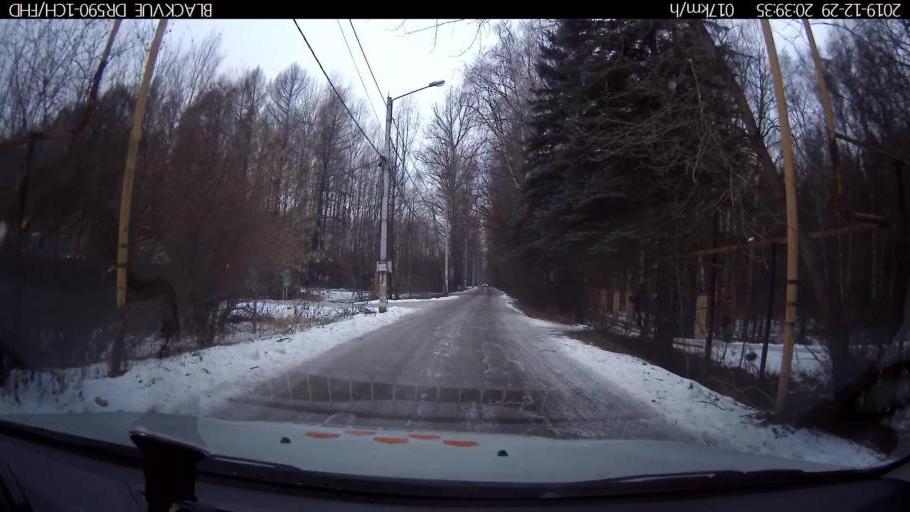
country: RU
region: Nizjnij Novgorod
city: Afonino
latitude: 56.1922
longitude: 44.0480
